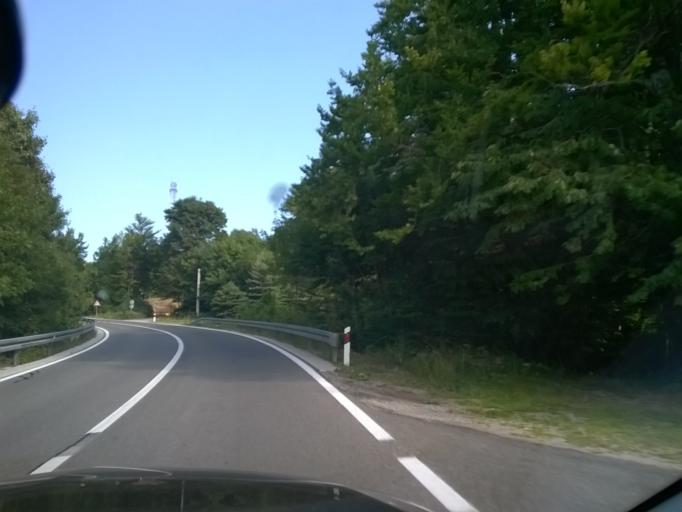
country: HR
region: Licko-Senjska
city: Karlobag
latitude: 44.5212
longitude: 15.1853
